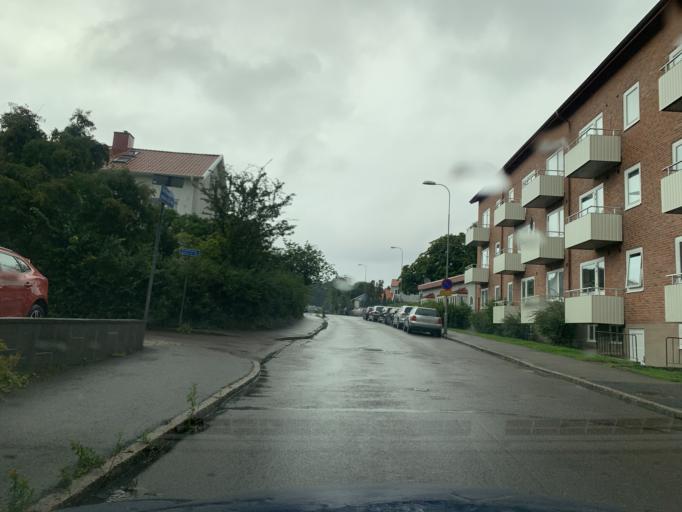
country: SE
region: Vaestra Goetaland
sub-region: Molndal
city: Moelndal
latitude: 57.7029
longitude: 12.0145
